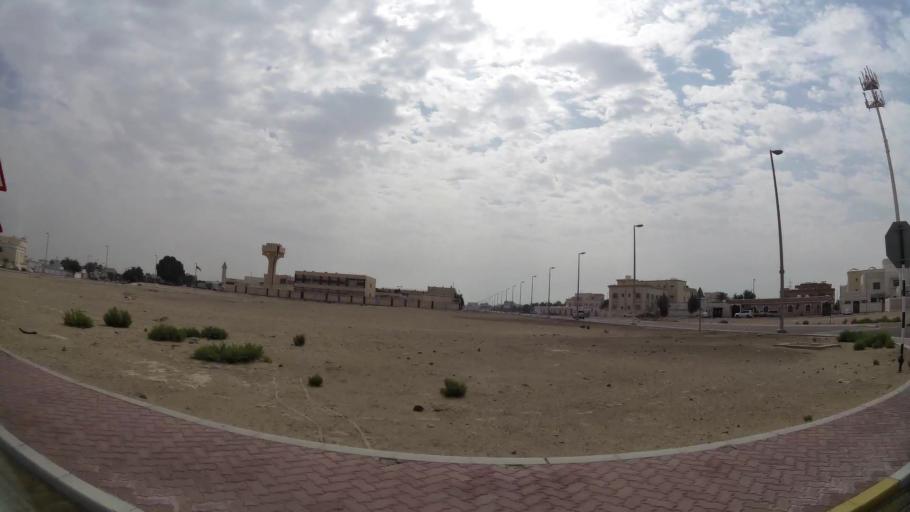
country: AE
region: Abu Dhabi
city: Abu Dhabi
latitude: 24.3194
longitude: 54.6381
